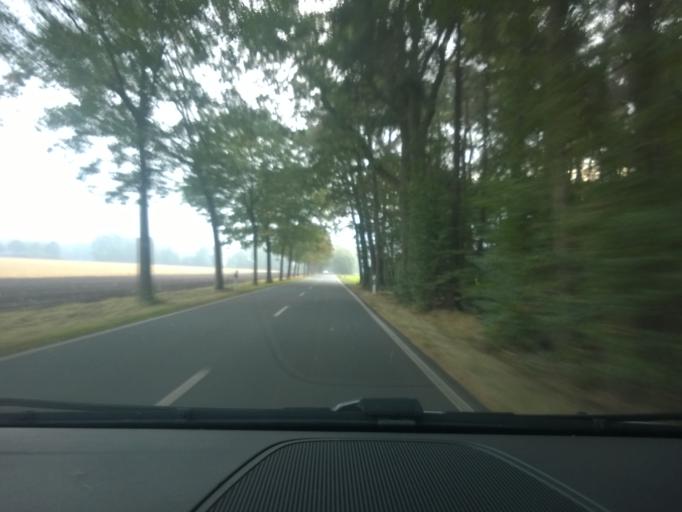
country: DE
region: North Rhine-Westphalia
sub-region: Regierungsbezirk Munster
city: Sudlohn
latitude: 51.9467
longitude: 6.9100
